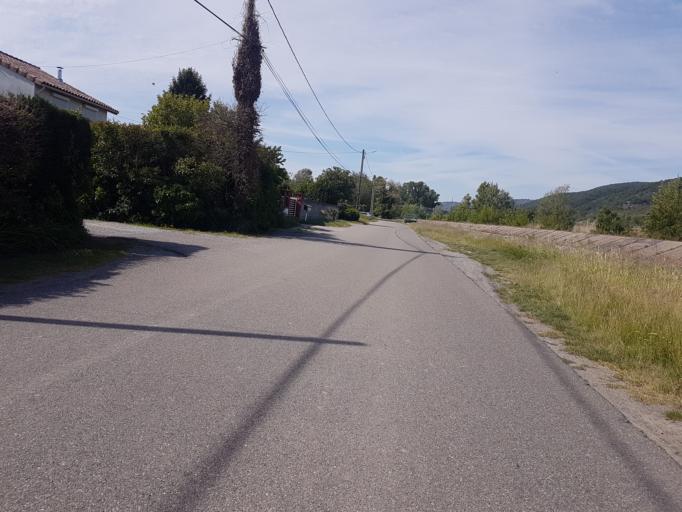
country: FR
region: Rhone-Alpes
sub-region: Departement de l'Ardeche
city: La Voulte-sur-Rhone
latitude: 44.7973
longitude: 4.7843
